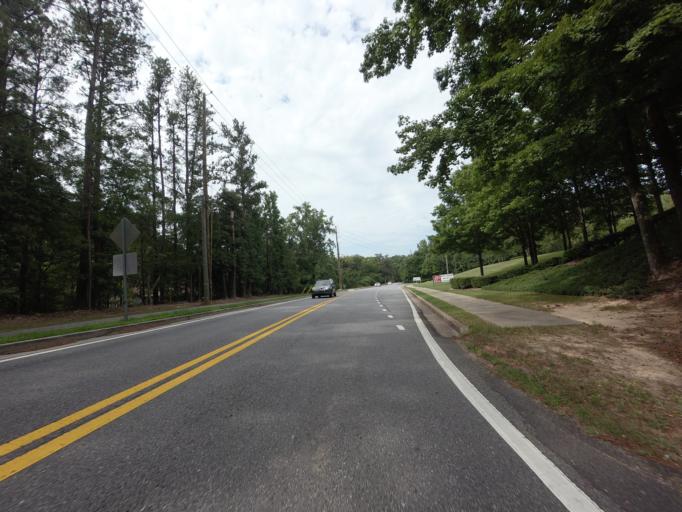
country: US
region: Georgia
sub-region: Gwinnett County
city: Duluth
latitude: 34.0501
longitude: -84.1343
